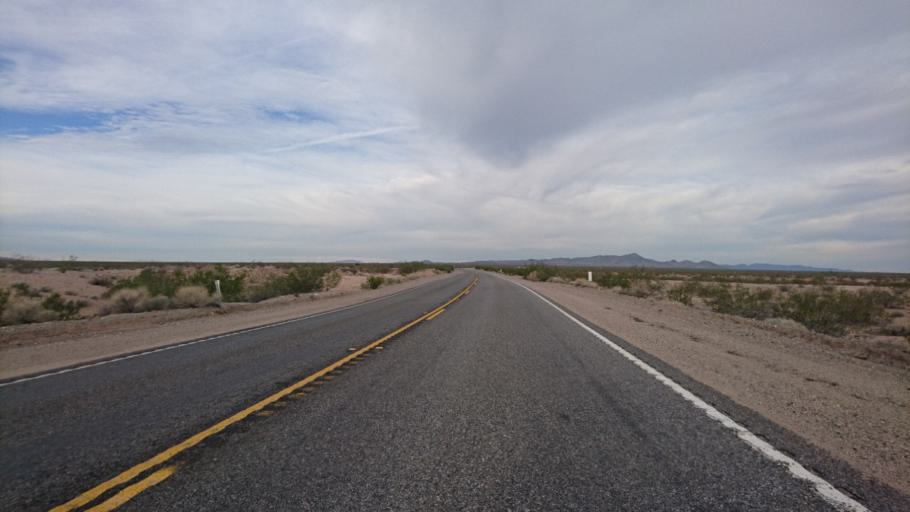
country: US
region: Arizona
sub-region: Mohave County
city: Willow Valley
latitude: 34.9387
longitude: -114.8101
